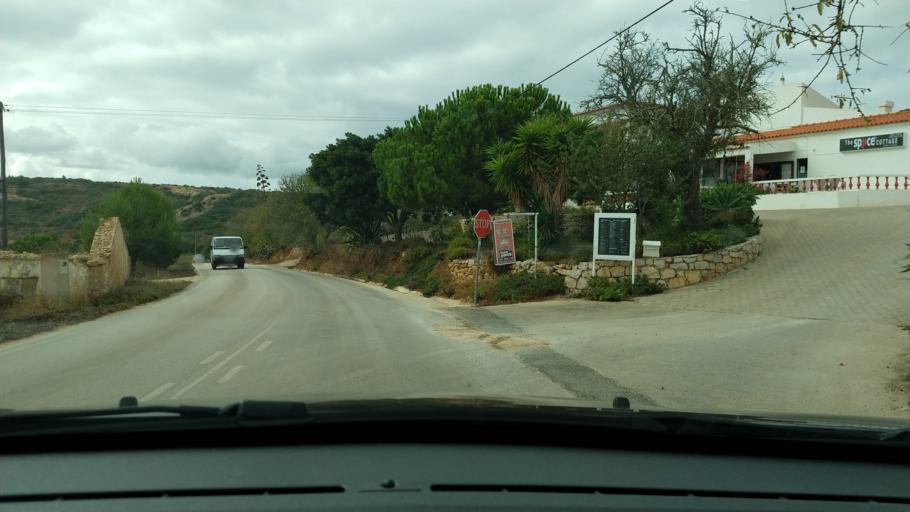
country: PT
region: Faro
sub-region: Lagos
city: Lagos
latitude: 37.0714
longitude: -8.7890
